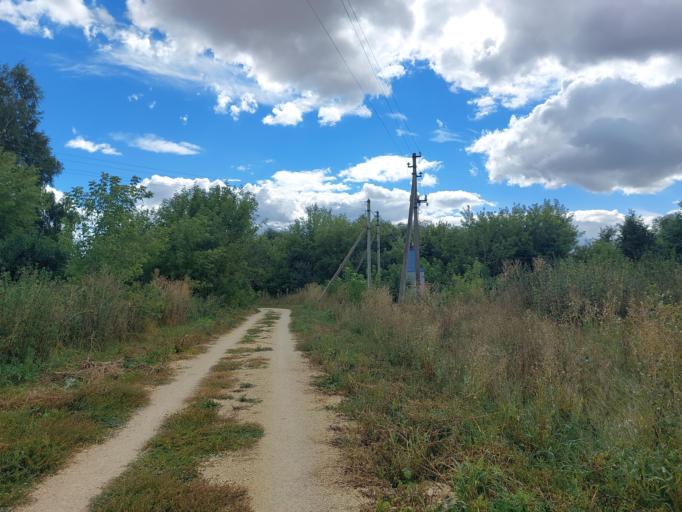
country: RU
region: Lipetsk
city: Terbuny
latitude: 52.2609
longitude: 38.2069
